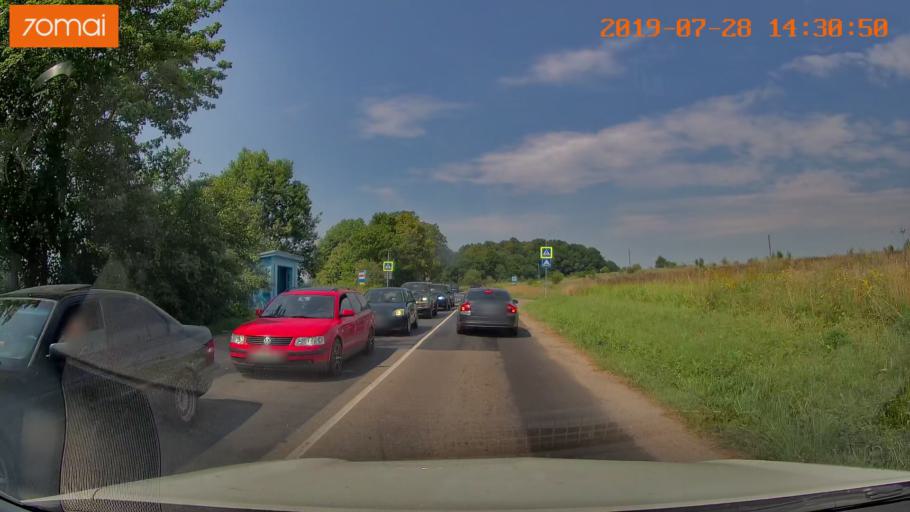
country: RU
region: Kaliningrad
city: Primorsk
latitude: 54.8035
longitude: 20.0551
